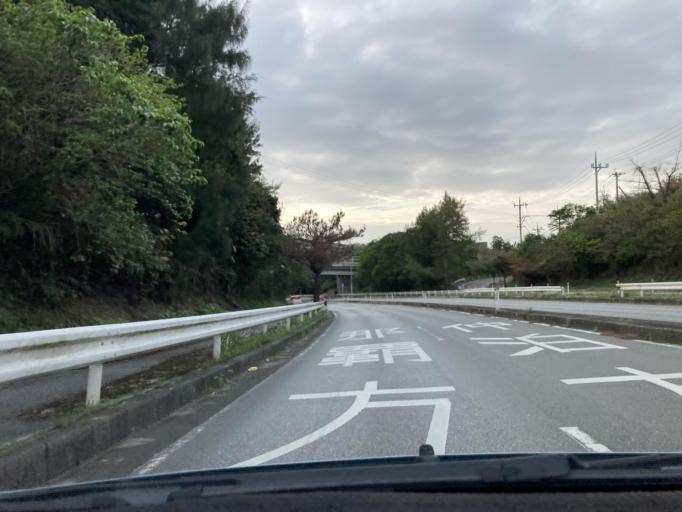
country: JP
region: Okinawa
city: Ishikawa
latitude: 26.4381
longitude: 127.8079
